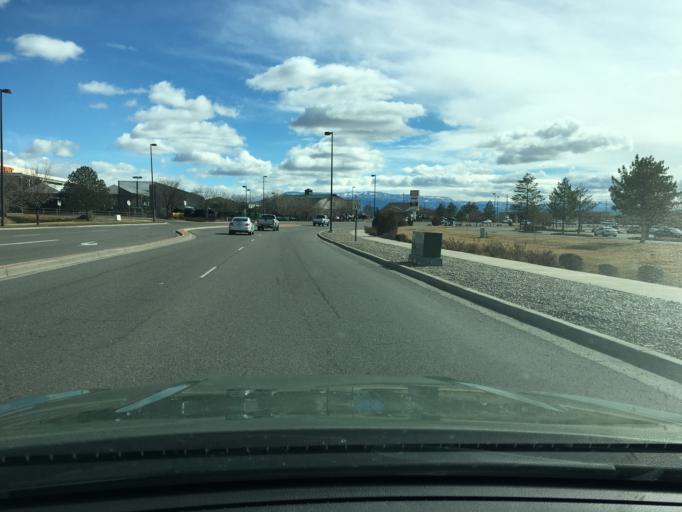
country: US
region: Colorado
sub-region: Mesa County
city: Redlands
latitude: 39.0947
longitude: -108.6024
